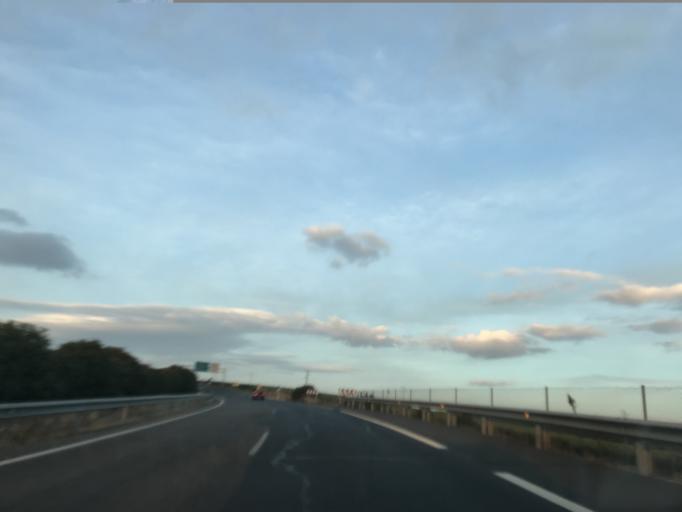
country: ES
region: Andalusia
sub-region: Province of Cordoba
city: La Victoria
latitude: 37.7547
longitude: -4.8331
